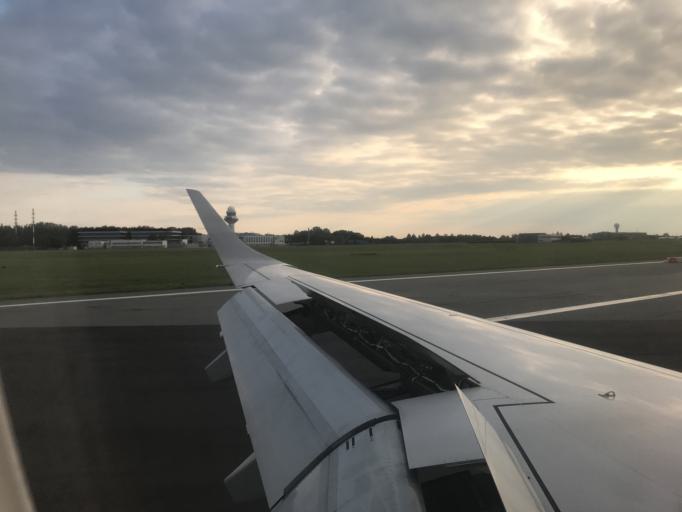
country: PL
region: Masovian Voivodeship
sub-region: Warszawa
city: Wlochy
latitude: 52.1659
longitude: 20.9668
